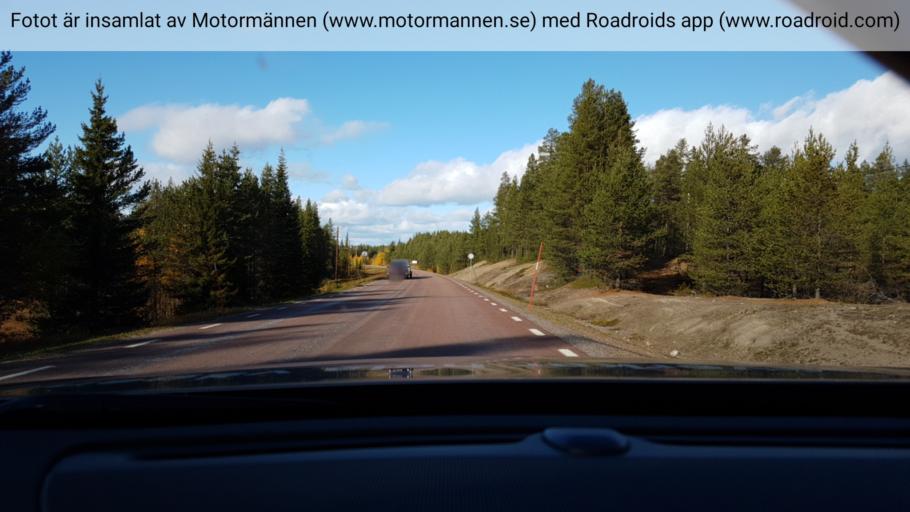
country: SE
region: Norrbotten
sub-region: Arjeplogs Kommun
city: Arjeplog
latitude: 66.0490
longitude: 18.0268
